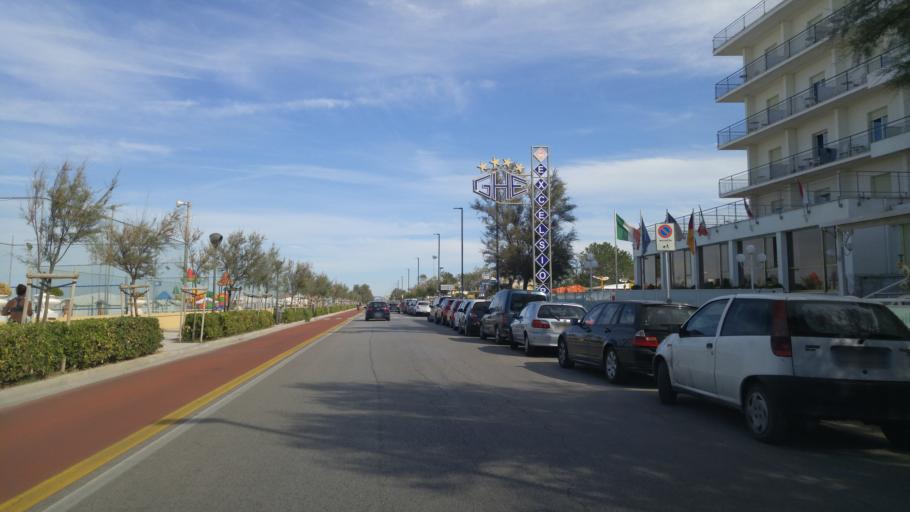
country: IT
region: The Marches
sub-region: Provincia di Ancona
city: Senigallia
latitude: 43.7065
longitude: 13.2378
